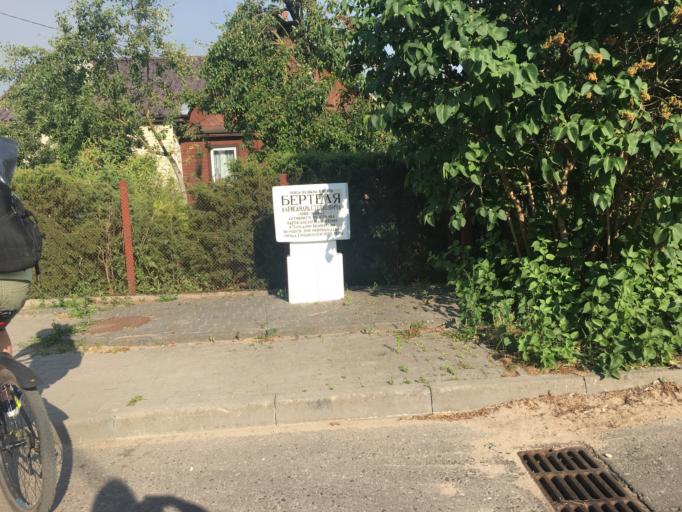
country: BY
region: Grodnenskaya
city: Hrodna
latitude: 53.6653
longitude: 23.8111
